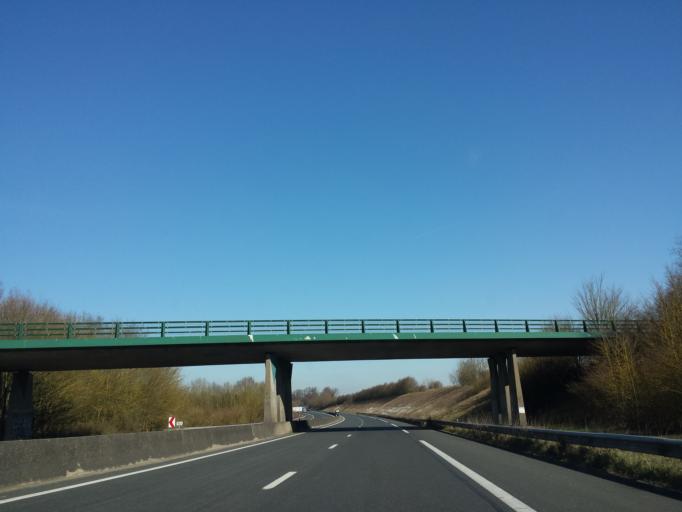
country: FR
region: Picardie
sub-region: Departement de l'Oise
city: Breteuil
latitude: 49.6123
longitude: 2.2079
